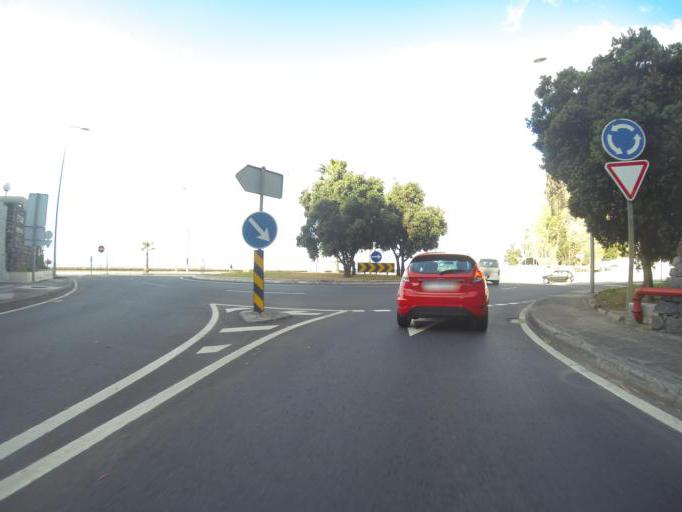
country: PT
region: Madeira
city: Ponta do Sol
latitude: 32.6780
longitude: -17.0808
